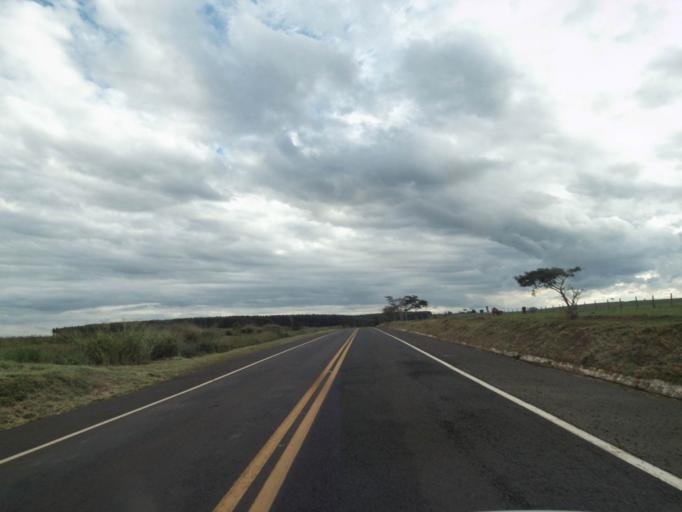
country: PY
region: Canindeyu
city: Salto del Guaira
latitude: -24.0839
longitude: -54.0734
